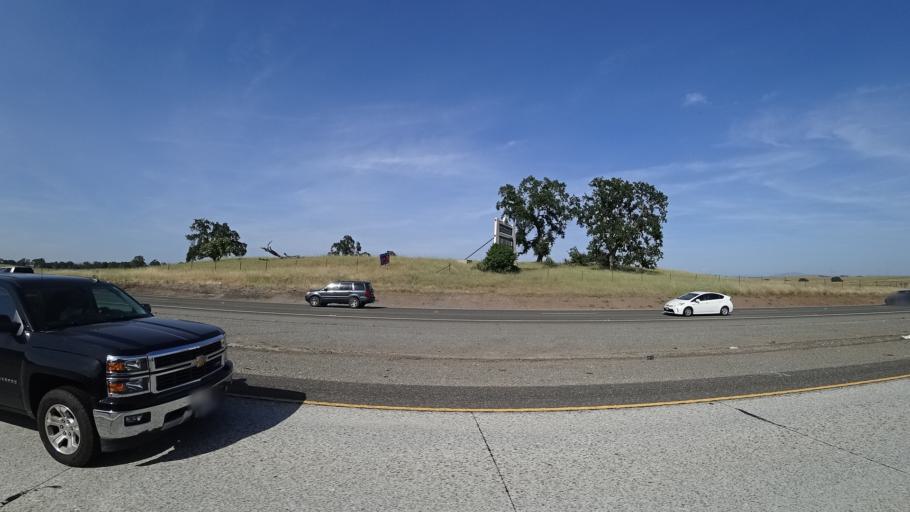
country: US
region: California
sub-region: Butte County
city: Durham
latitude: 39.6829
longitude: -121.7655
